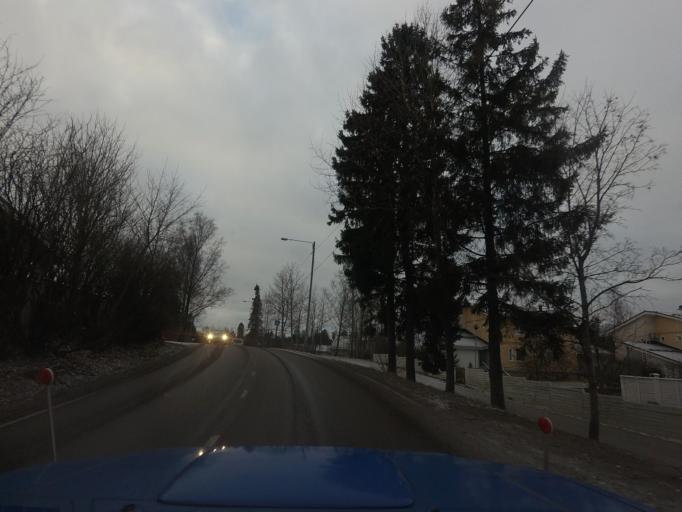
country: FI
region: Uusimaa
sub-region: Helsinki
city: Espoo
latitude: 60.2145
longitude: 24.6463
